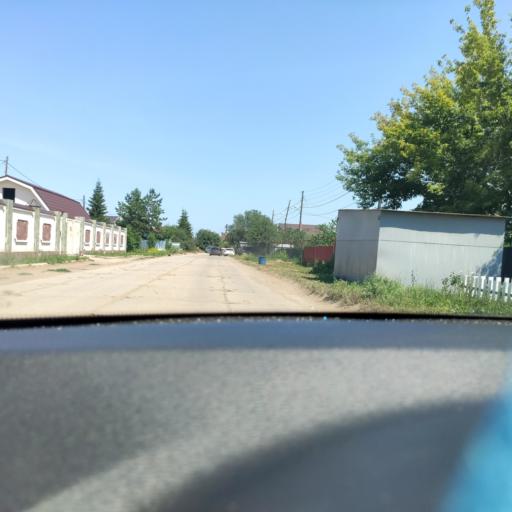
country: RU
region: Samara
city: Smyshlyayevka
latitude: 53.2226
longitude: 50.3386
